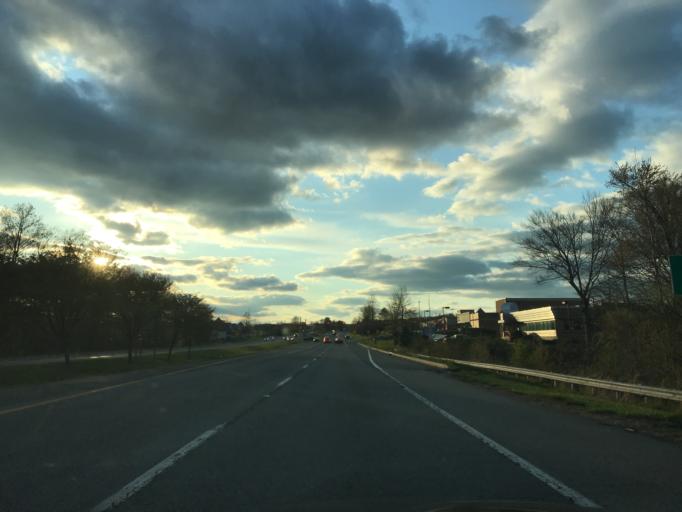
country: US
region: Maryland
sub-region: Harford County
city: Bel Air
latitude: 39.5227
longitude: -76.3478
